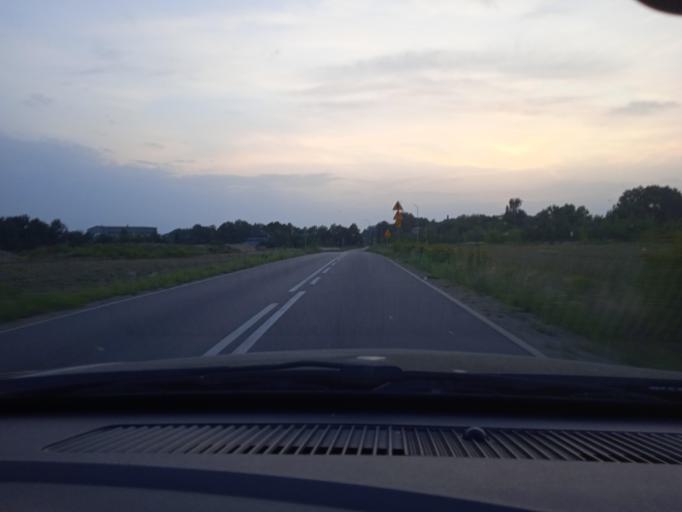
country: PL
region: Masovian Voivodeship
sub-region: Powiat nowodworski
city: Pomiechowek
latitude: 52.4649
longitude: 20.7028
